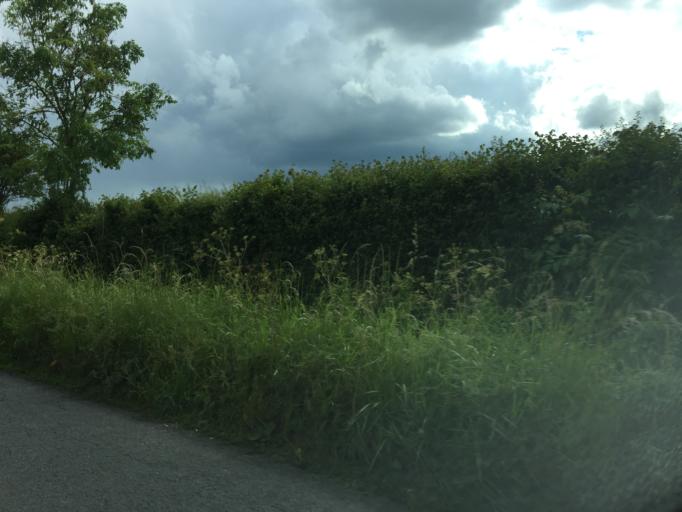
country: GB
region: England
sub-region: Wiltshire
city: Purton
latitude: 51.6077
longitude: -1.8488
